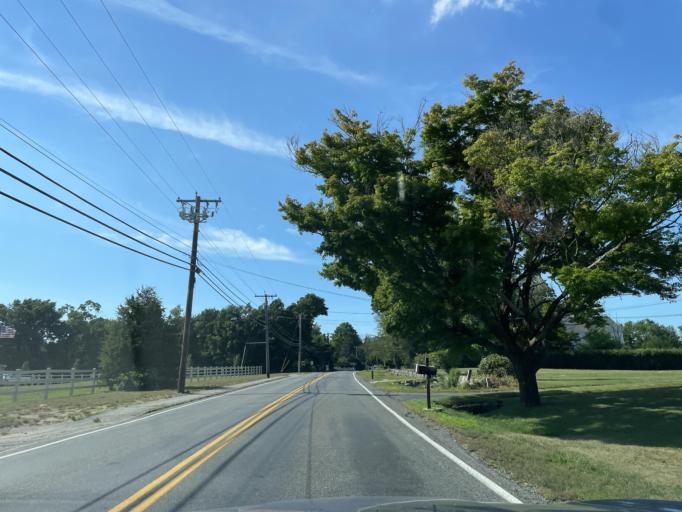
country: US
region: Massachusetts
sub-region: Worcester County
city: Mendon
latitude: 42.1149
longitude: -71.5618
